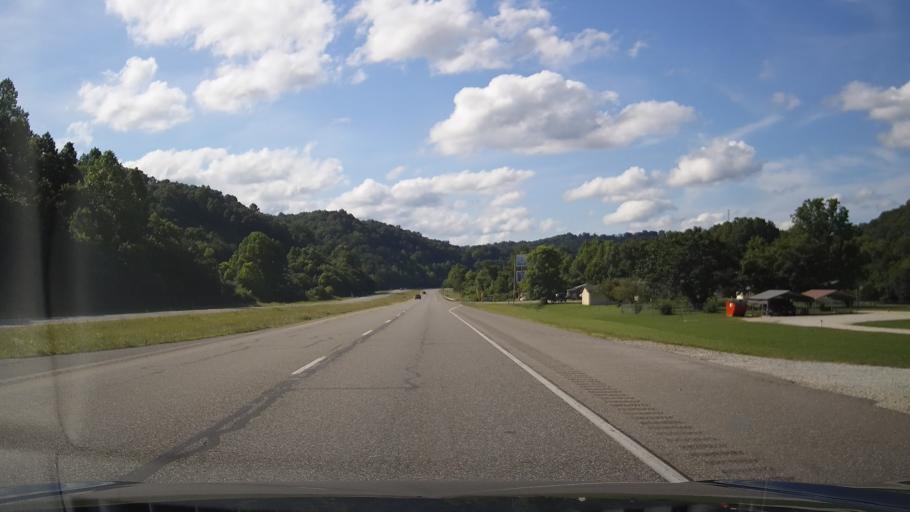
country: US
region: Kentucky
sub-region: Lawrence County
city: Louisa
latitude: 38.1567
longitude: -82.6421
